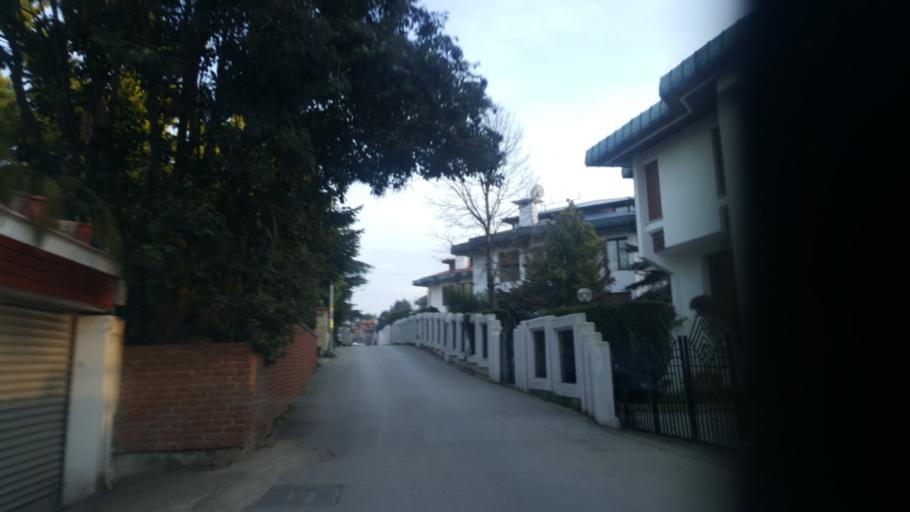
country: TR
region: Istanbul
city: Icmeler
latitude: 40.8181
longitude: 29.2718
